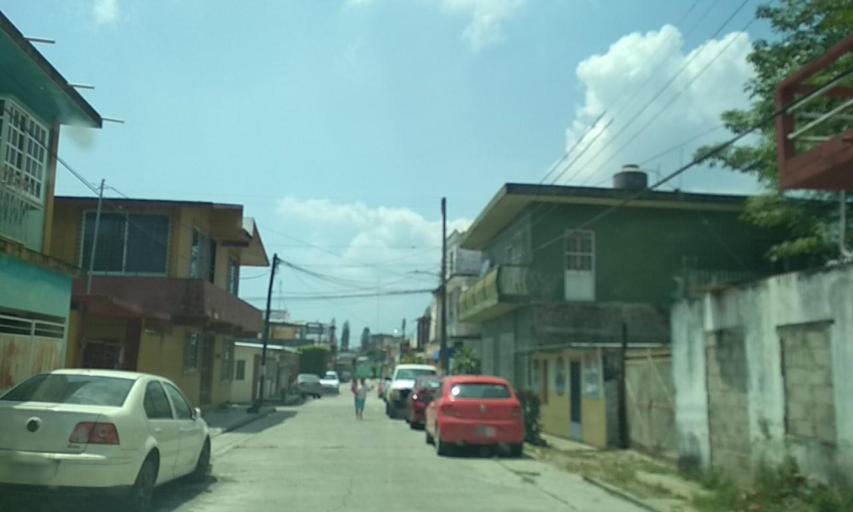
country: MX
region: Veracruz
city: Las Choapas
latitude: 17.9113
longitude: -94.0914
